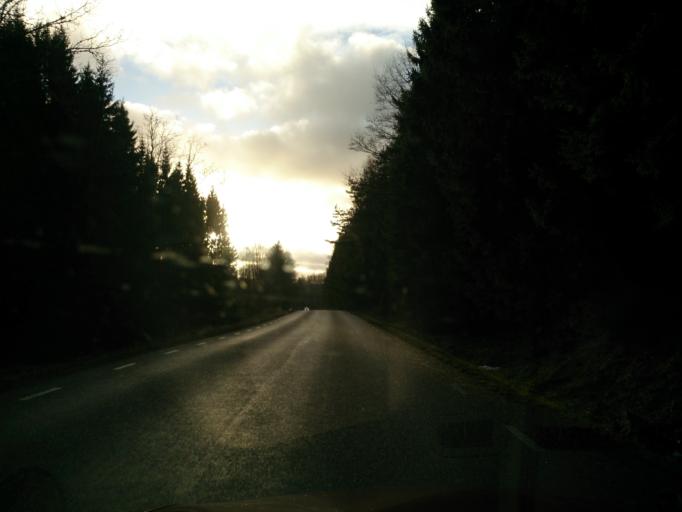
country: SE
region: OEstergoetland
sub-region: Atvidabergs Kommun
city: Atvidaberg
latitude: 58.2985
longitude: 16.0092
